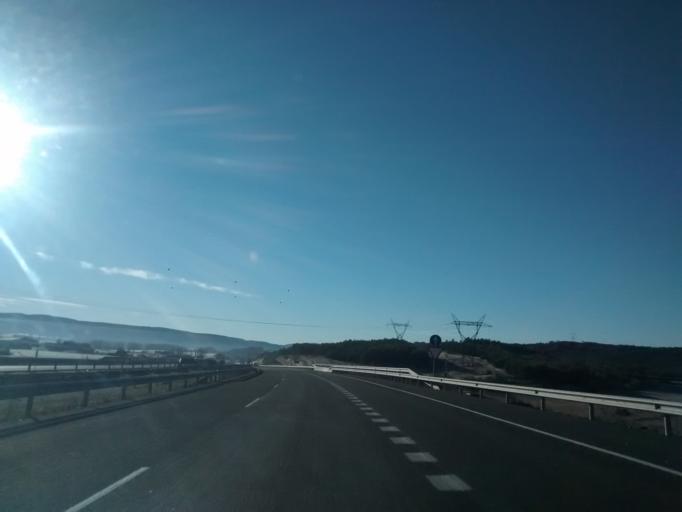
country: ES
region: Castille and Leon
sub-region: Provincia de Palencia
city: Aguilar de Campoo
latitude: 42.7507
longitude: -4.2934
